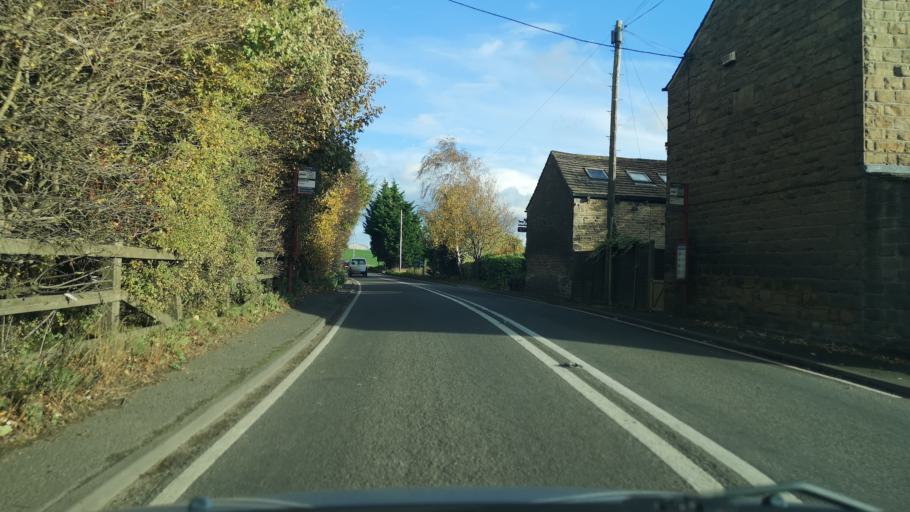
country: GB
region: England
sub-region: City and Borough of Wakefield
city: Middlestown
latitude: 53.6305
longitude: -1.6170
